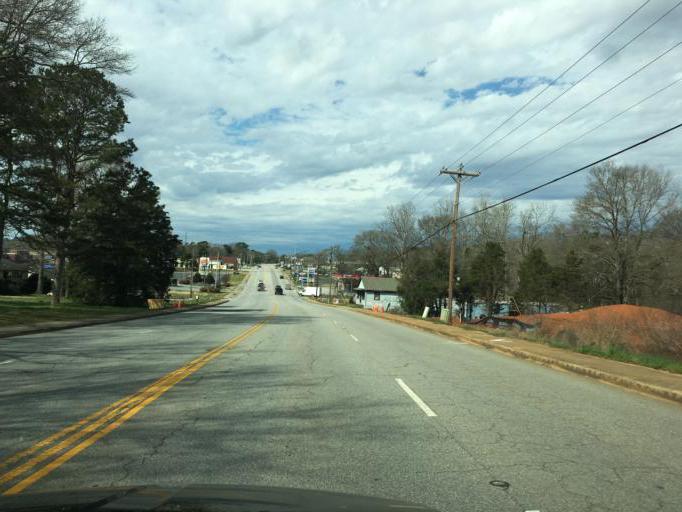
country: US
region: South Carolina
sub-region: Greenville County
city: Fountain Inn
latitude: 34.7011
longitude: -82.2142
